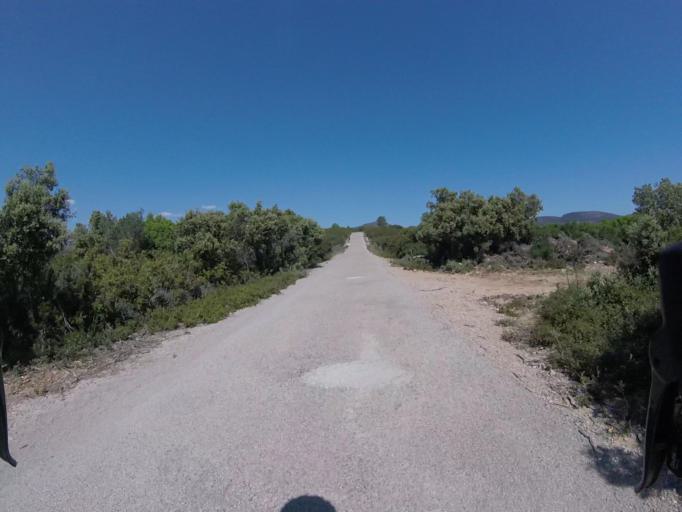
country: ES
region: Valencia
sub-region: Provincia de Castello
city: Sierra-Engarceran
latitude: 40.2313
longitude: -0.0247
